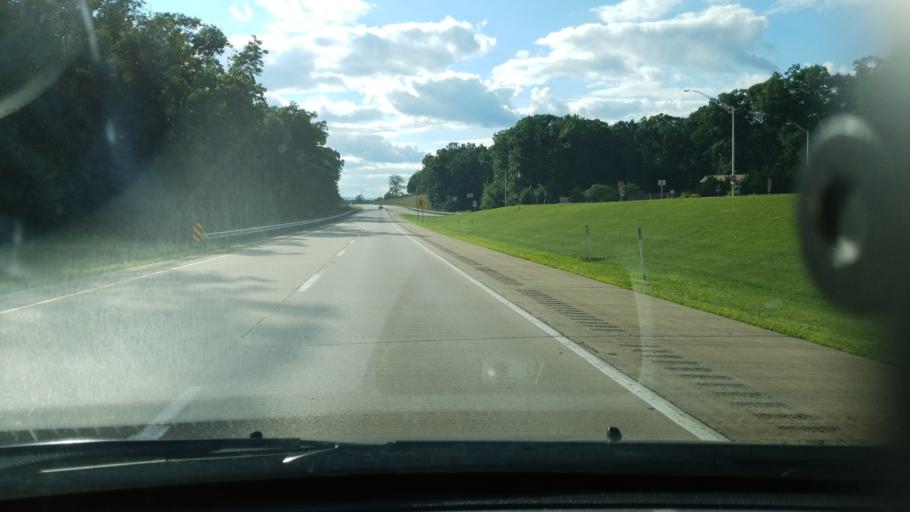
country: US
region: Pennsylvania
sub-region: Northumberland County
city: Riverside
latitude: 40.9899
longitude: -76.7263
